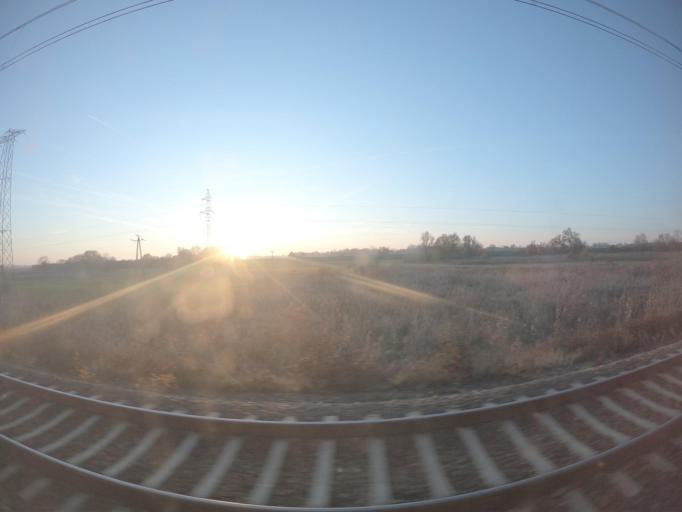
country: PL
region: Lubusz
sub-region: Powiat gorzowski
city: Kostrzyn nad Odra
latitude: 52.5682
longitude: 14.6458
